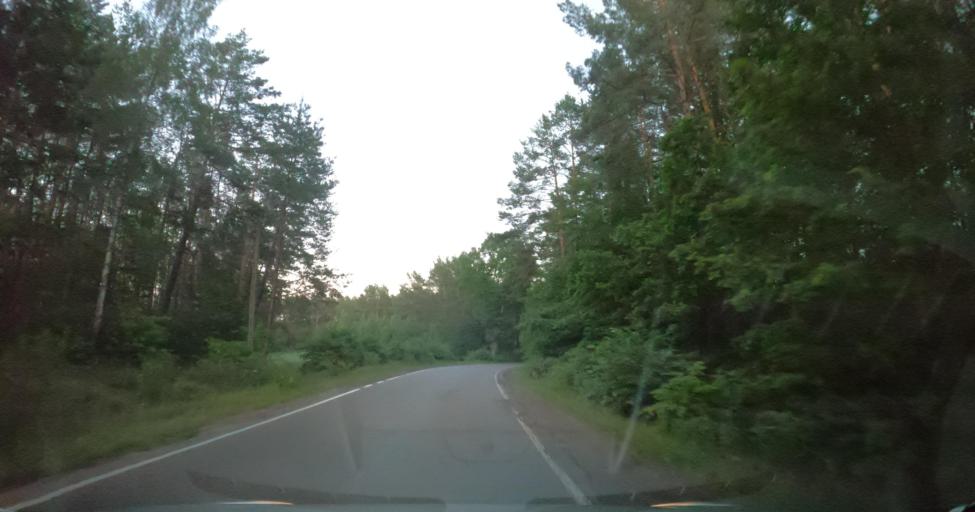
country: PL
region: Pomeranian Voivodeship
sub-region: Powiat wejherowski
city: Luzino
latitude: 54.4741
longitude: 18.0916
